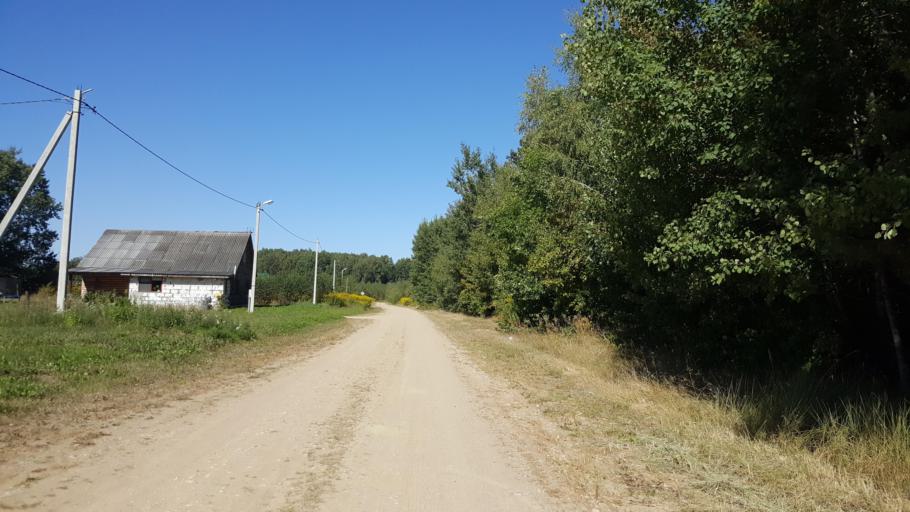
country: BY
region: Brest
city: Vysokaye
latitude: 52.2522
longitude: 23.5018
